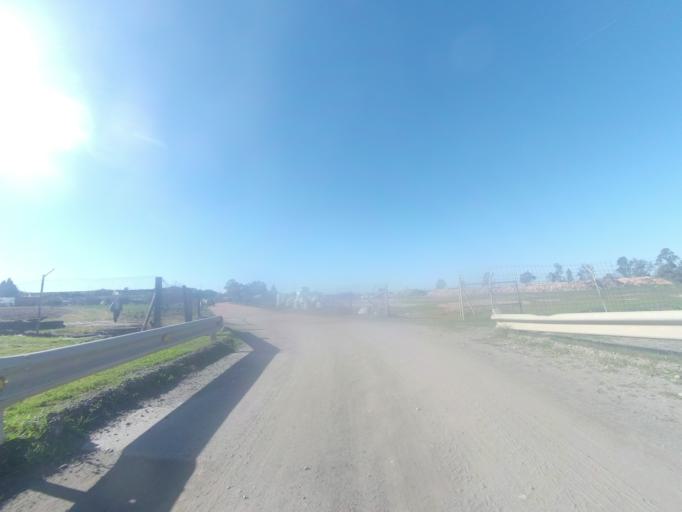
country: ES
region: Andalusia
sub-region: Provincia de Huelva
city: Palos de la Frontera
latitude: 37.2335
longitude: -6.8987
